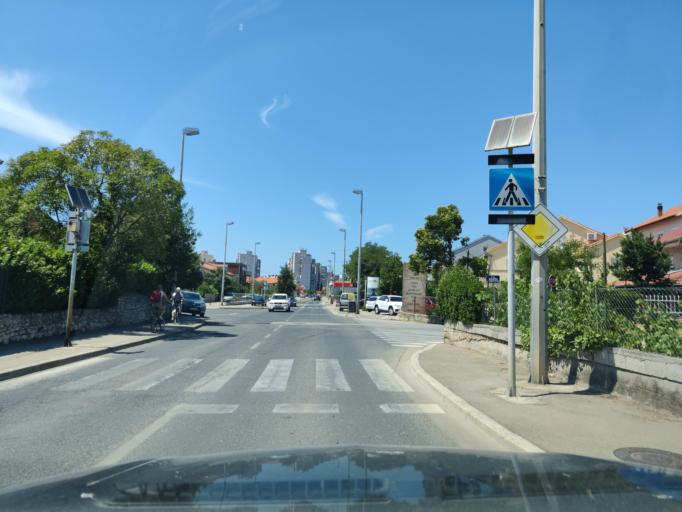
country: HR
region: Zadarska
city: Zadar
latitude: 44.1061
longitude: 15.2524
